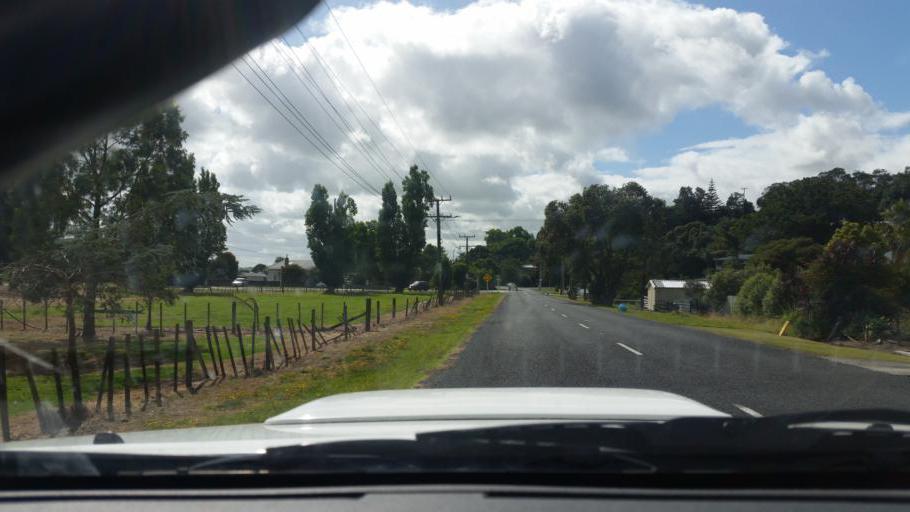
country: NZ
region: Northland
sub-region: Kaipara District
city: Dargaville
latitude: -35.9566
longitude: 173.8640
